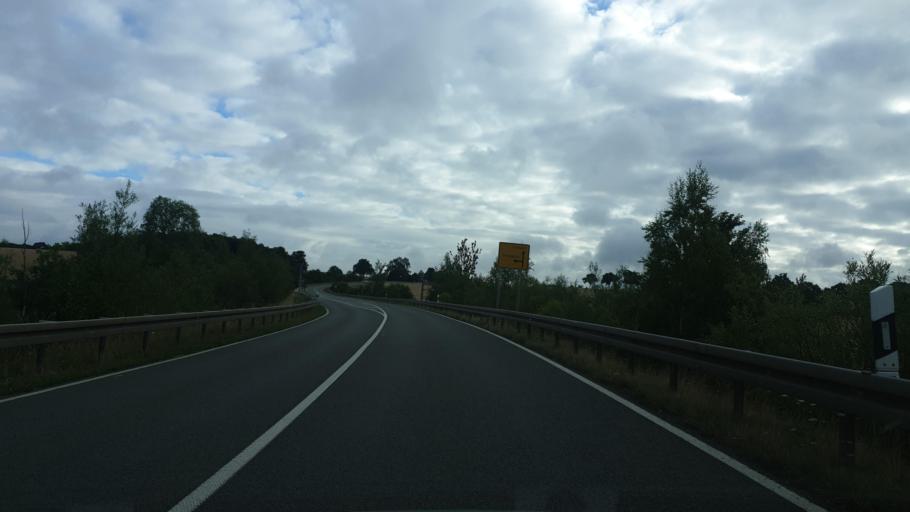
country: DE
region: Saxony
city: Limbach
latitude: 50.5709
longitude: 12.2177
